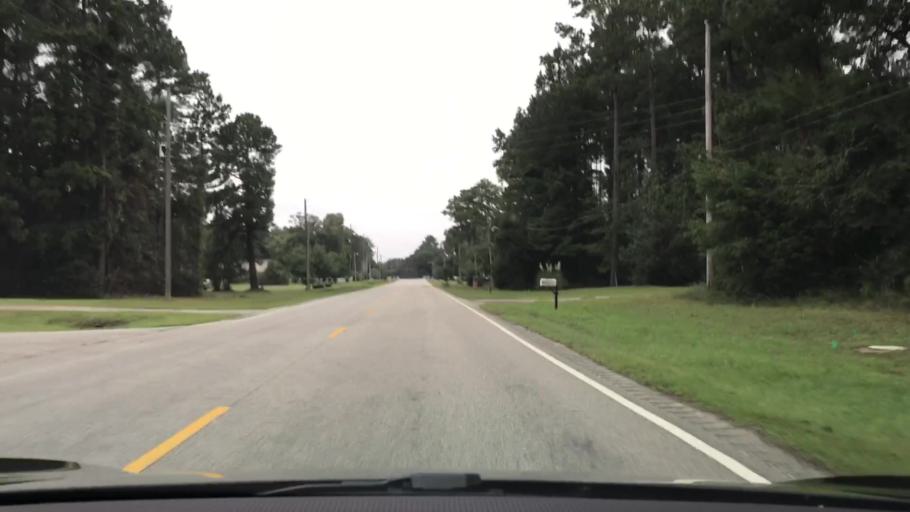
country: US
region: Alabama
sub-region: Coffee County
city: Elba
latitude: 31.3865
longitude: -86.0852
